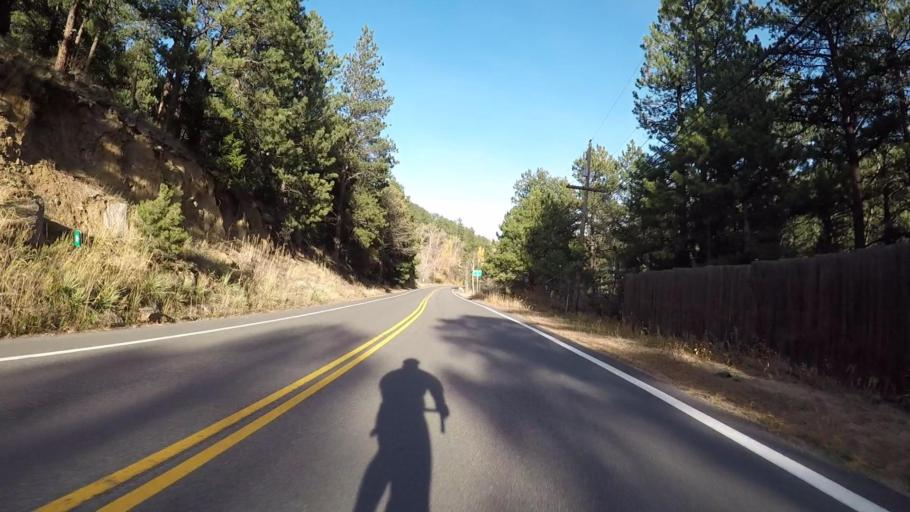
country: US
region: Colorado
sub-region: Boulder County
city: Boulder
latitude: 40.0804
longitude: -105.3794
